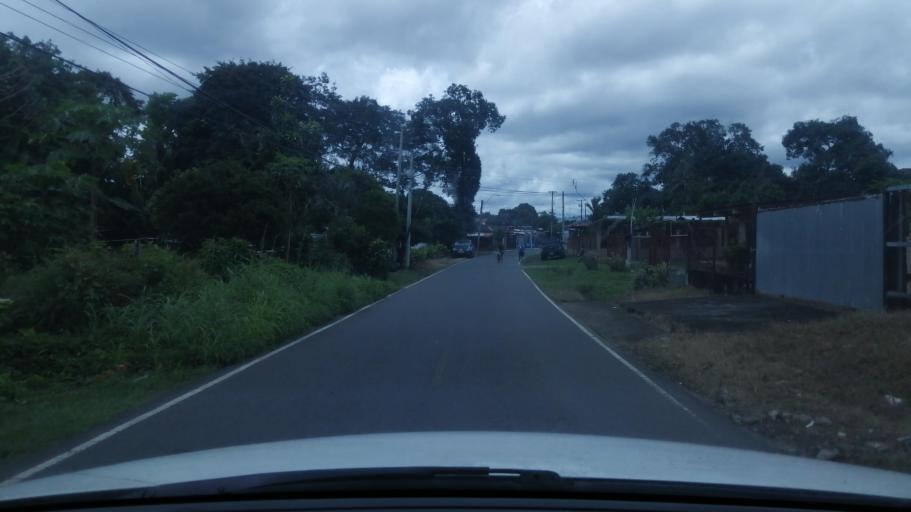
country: PA
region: Chiriqui
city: David
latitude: 8.4207
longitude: -82.4279
